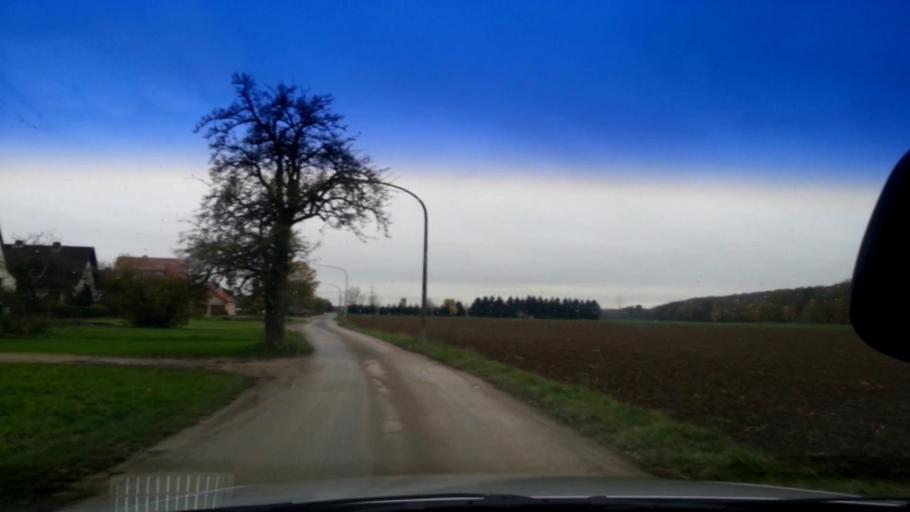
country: DE
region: Bavaria
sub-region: Upper Franconia
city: Schesslitz
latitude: 49.9734
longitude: 11.0255
